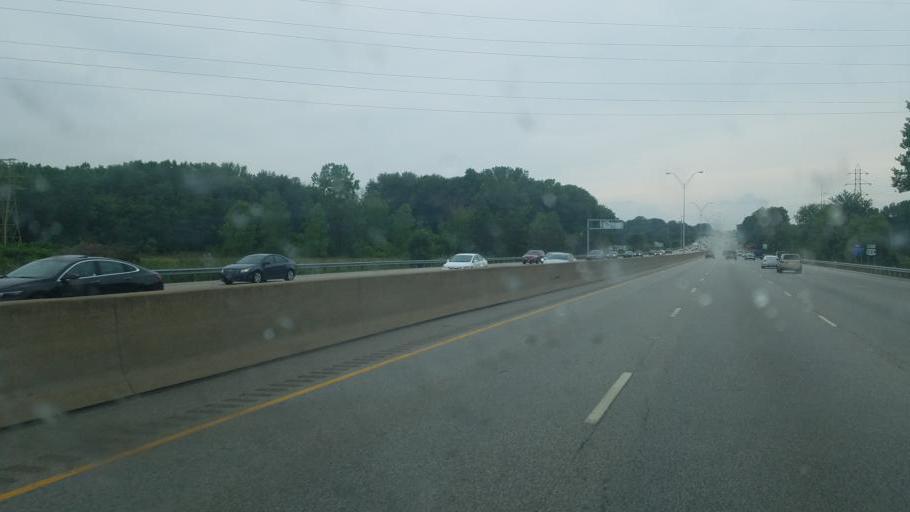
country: US
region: Ohio
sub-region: Summit County
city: Portage Lakes
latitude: 41.0257
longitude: -81.5314
